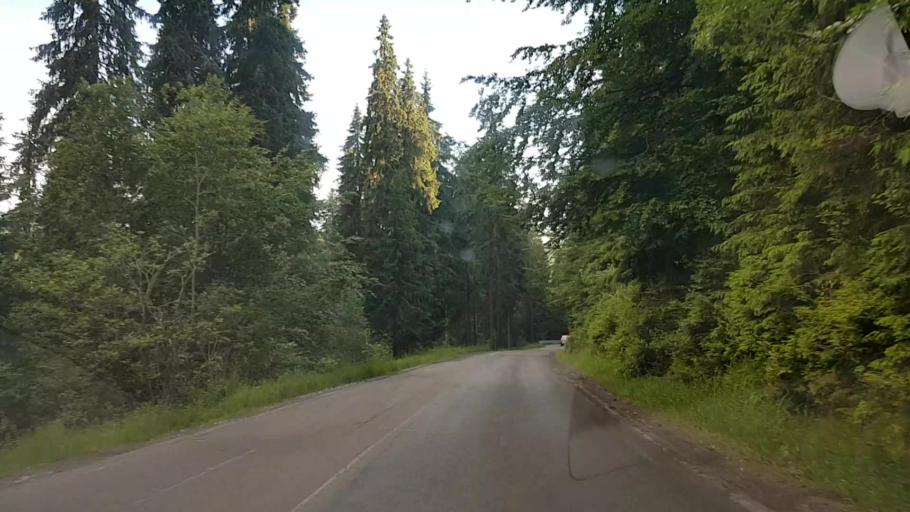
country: RO
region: Harghita
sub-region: Comuna Varsag
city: Varsag
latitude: 46.6483
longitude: 25.2884
